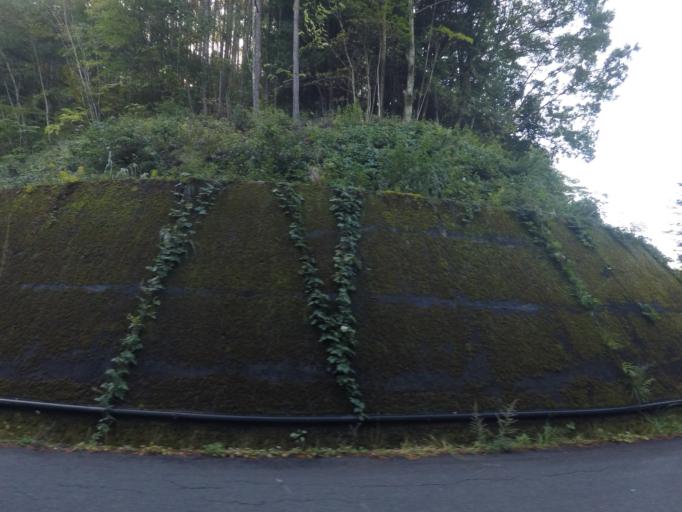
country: JP
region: Nagano
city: Tatsuno
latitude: 35.9704
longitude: 137.7739
